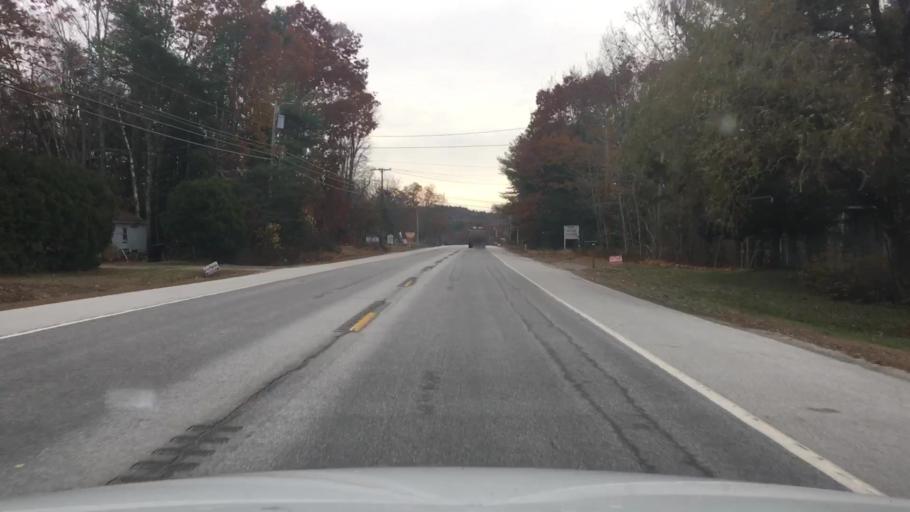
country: US
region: Maine
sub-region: Hancock County
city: Orland
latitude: 44.5654
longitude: -68.7169
